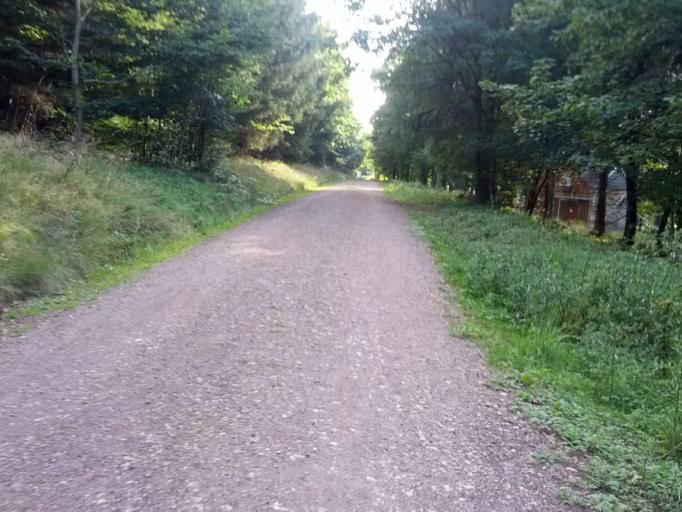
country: DE
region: Thuringia
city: Eisenach
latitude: 50.9340
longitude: 10.3210
